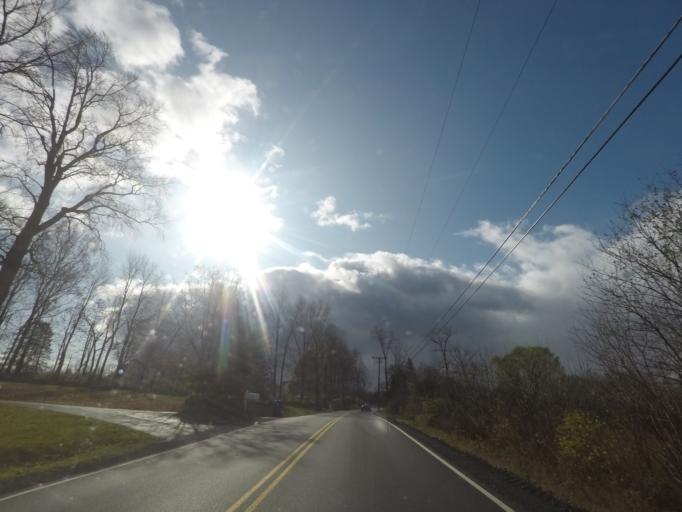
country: US
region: New York
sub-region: Saratoga County
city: Country Knolls
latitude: 42.9359
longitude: -73.8515
